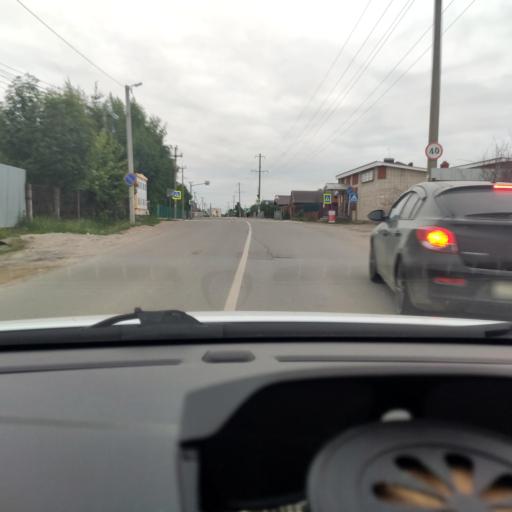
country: RU
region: Tatarstan
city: Vysokaya Gora
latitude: 55.9165
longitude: 49.3216
